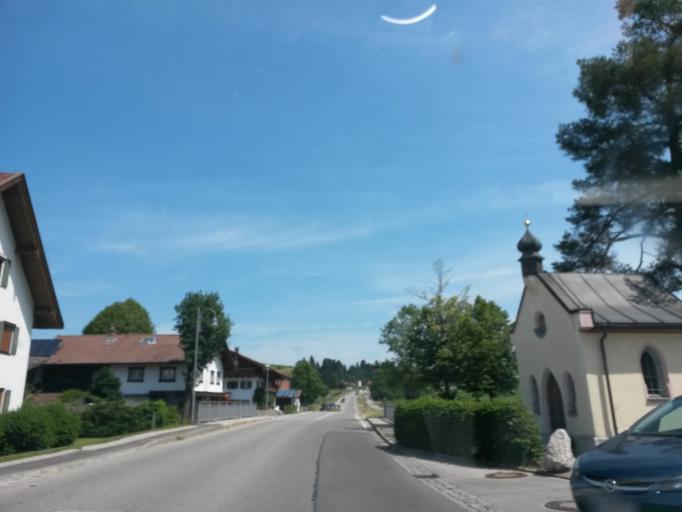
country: DE
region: Bavaria
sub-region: Swabia
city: Halblech
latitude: 47.6444
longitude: 10.8281
